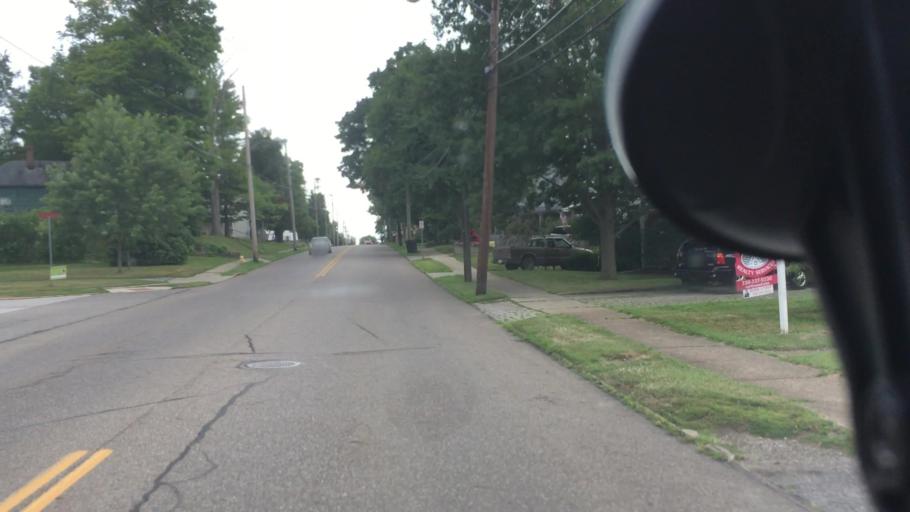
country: US
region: Ohio
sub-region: Columbiana County
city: Salem
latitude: 40.9083
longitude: -80.8493
